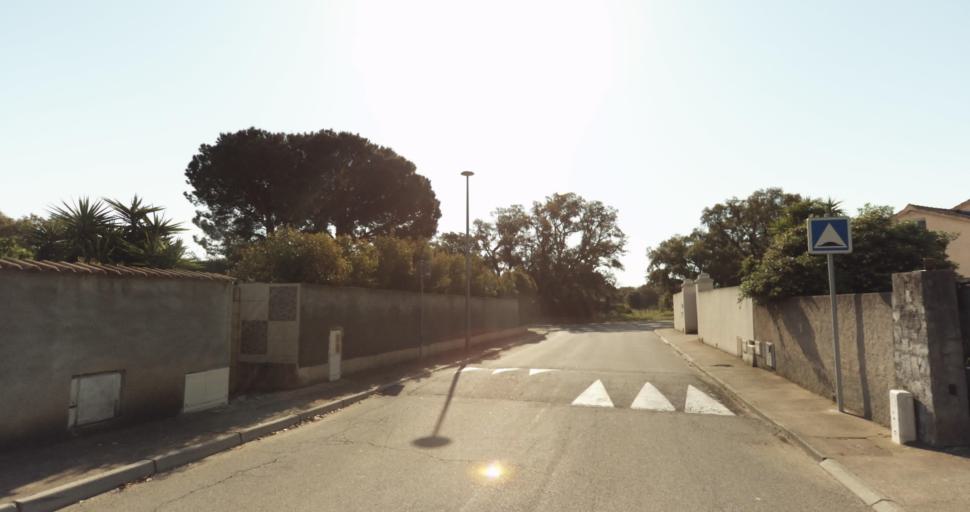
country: FR
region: Corsica
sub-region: Departement de la Haute-Corse
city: Biguglia
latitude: 42.6356
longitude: 9.4336
